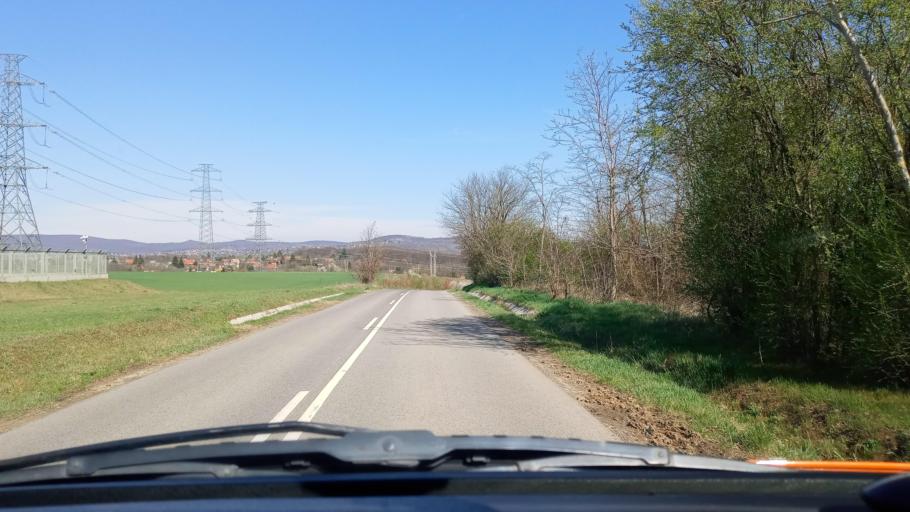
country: HU
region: Baranya
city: Kozarmisleny
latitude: 46.0784
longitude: 18.3080
